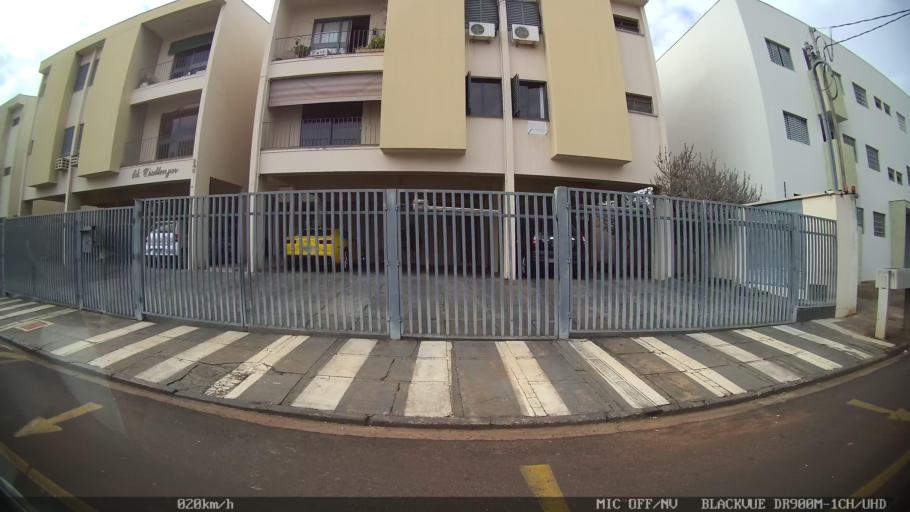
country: BR
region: Sao Paulo
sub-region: Sao Jose Do Rio Preto
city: Sao Jose do Rio Preto
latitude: -20.8304
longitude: -49.3997
